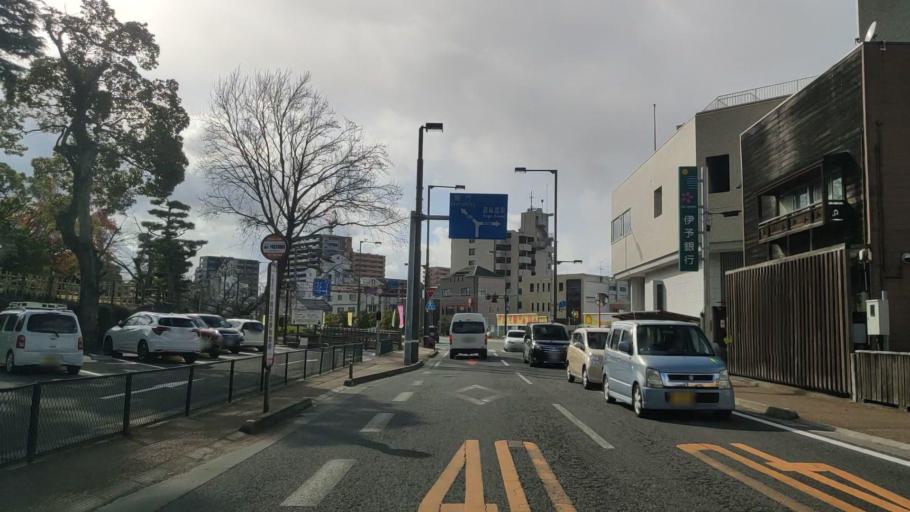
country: JP
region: Ehime
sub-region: Shikoku-chuo Shi
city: Matsuyama
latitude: 33.8498
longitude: 132.7858
